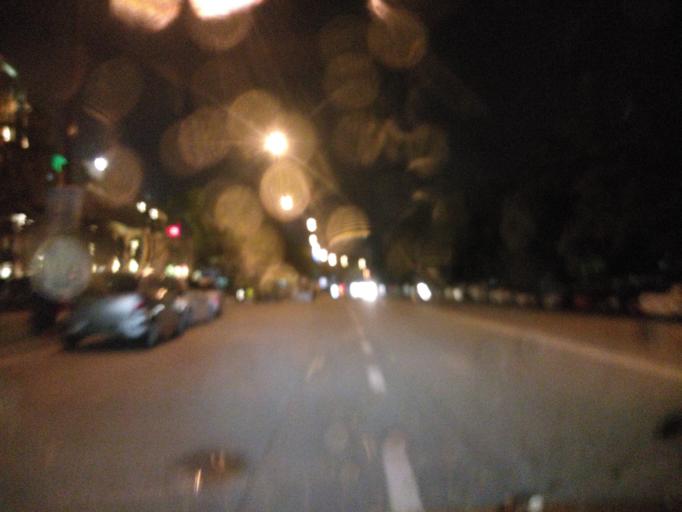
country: MY
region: Penang
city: Perai
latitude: 5.3995
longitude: 100.3974
